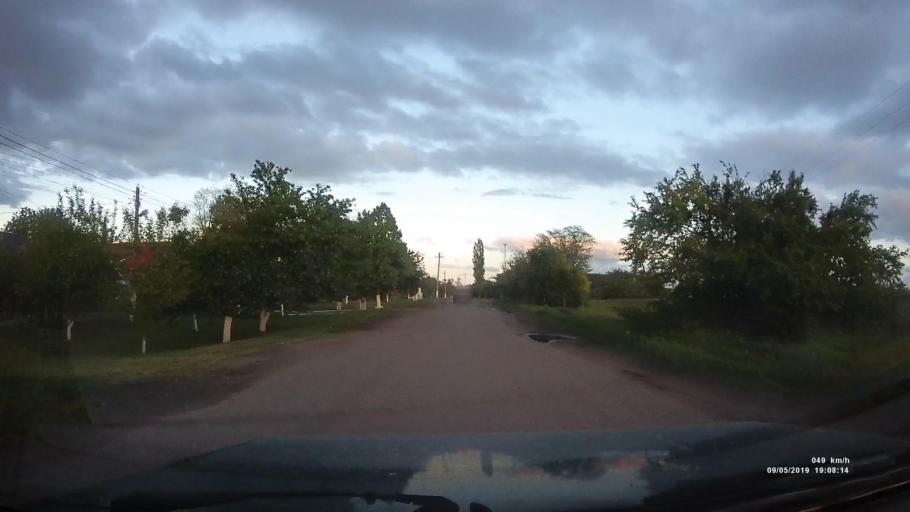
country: RU
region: Krasnodarskiy
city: Kanelovskaya
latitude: 46.7304
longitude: 39.2023
